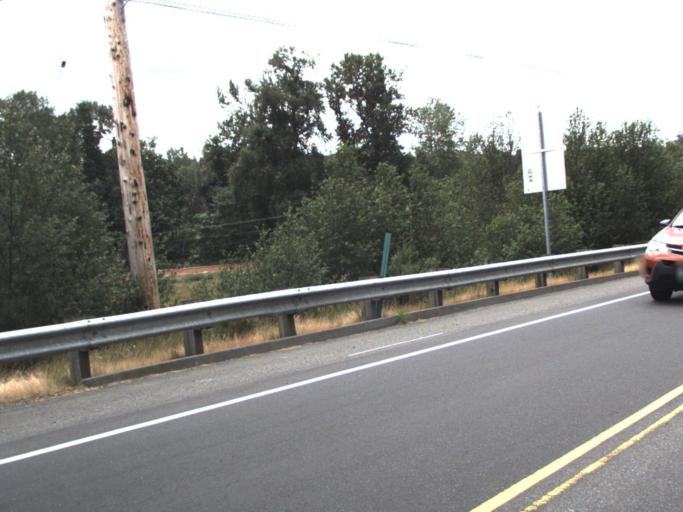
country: US
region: Washington
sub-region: Whatcom County
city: Ferndale
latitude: 48.8916
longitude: -122.5990
